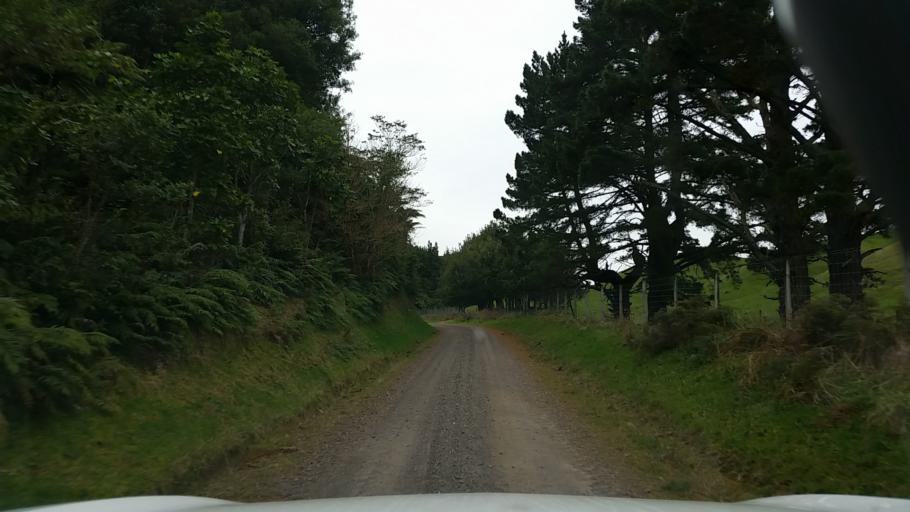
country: NZ
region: Bay of Plenty
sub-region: Rotorua District
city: Rotorua
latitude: -38.1578
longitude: 176.3708
